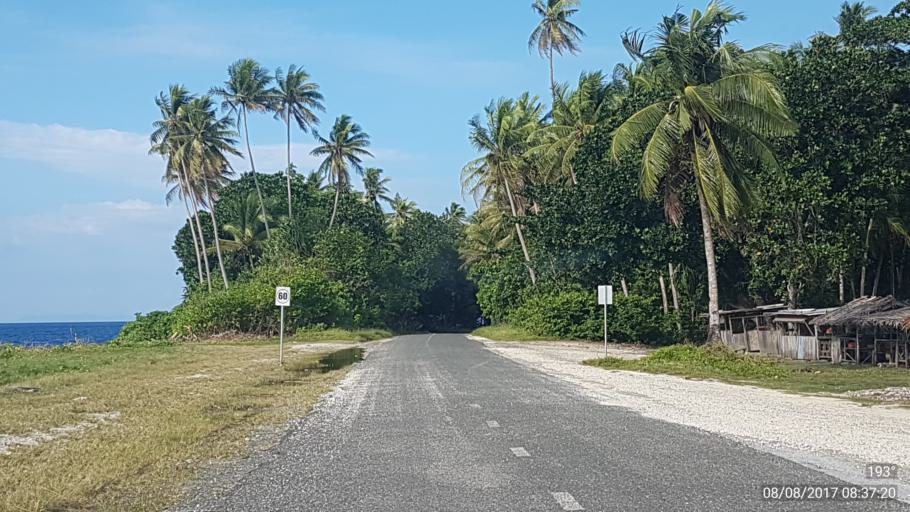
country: PG
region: Manus
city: Lorengau
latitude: -2.0748
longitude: 147.4276
